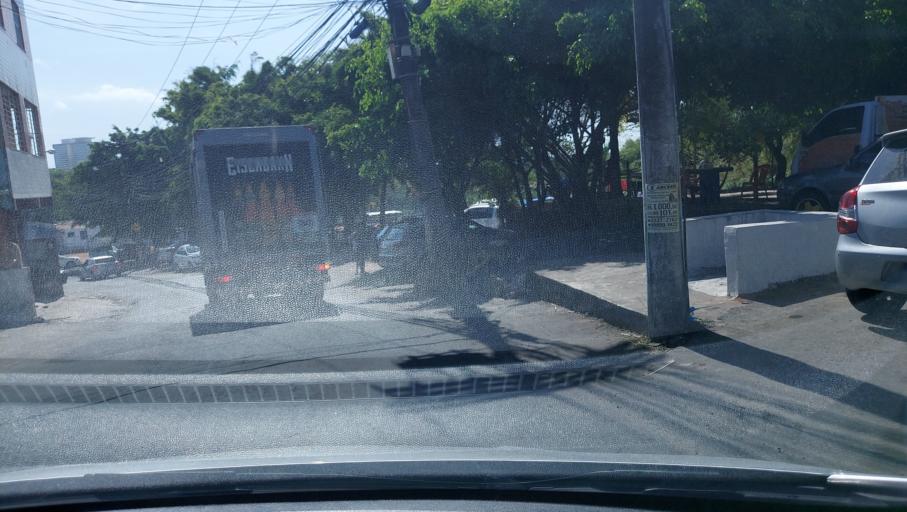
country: BR
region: Bahia
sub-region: Salvador
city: Salvador
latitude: -12.9769
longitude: -38.4410
